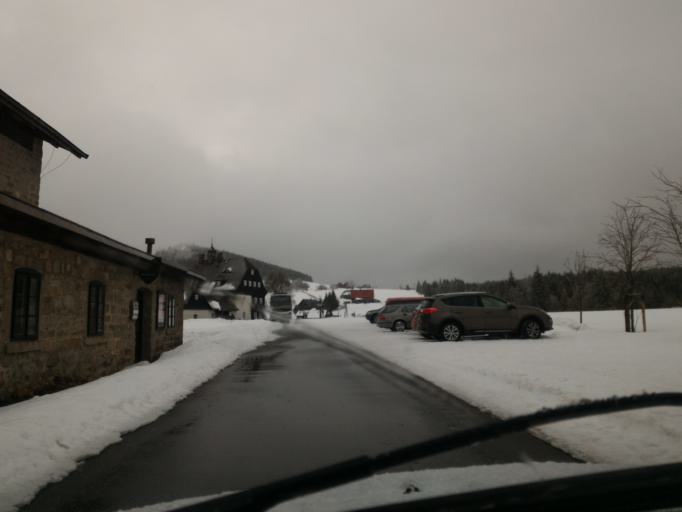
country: CZ
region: Liberecky
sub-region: Okres Jablonec nad Nisou
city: Korenov
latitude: 50.8191
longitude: 15.3442
